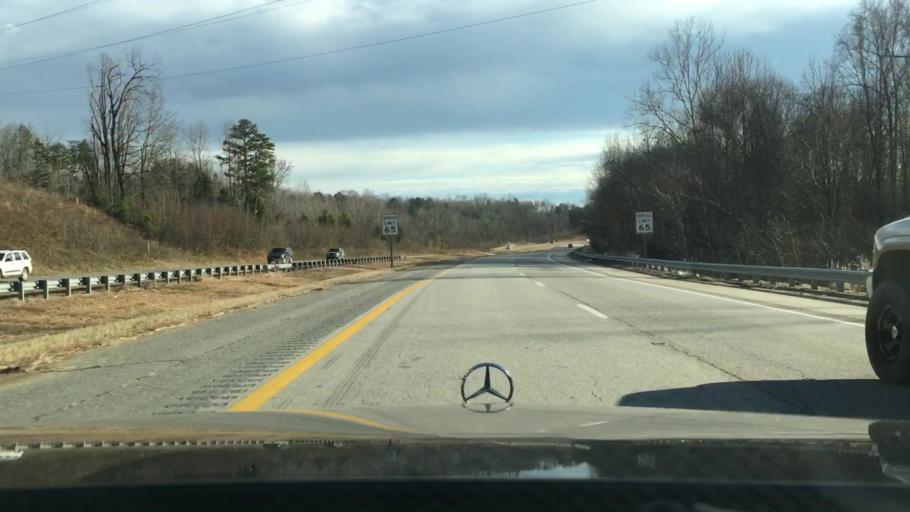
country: US
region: Virginia
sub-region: City of Danville
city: Danville
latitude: 36.6083
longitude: -79.3585
